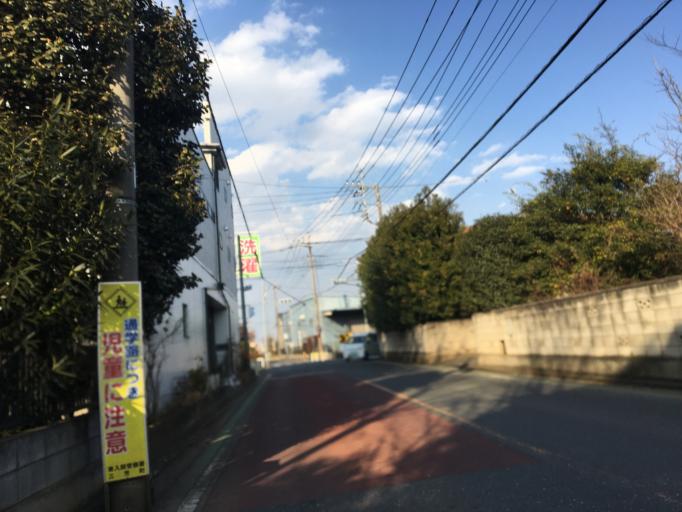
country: JP
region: Saitama
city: Oi
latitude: 35.8244
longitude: 139.5438
